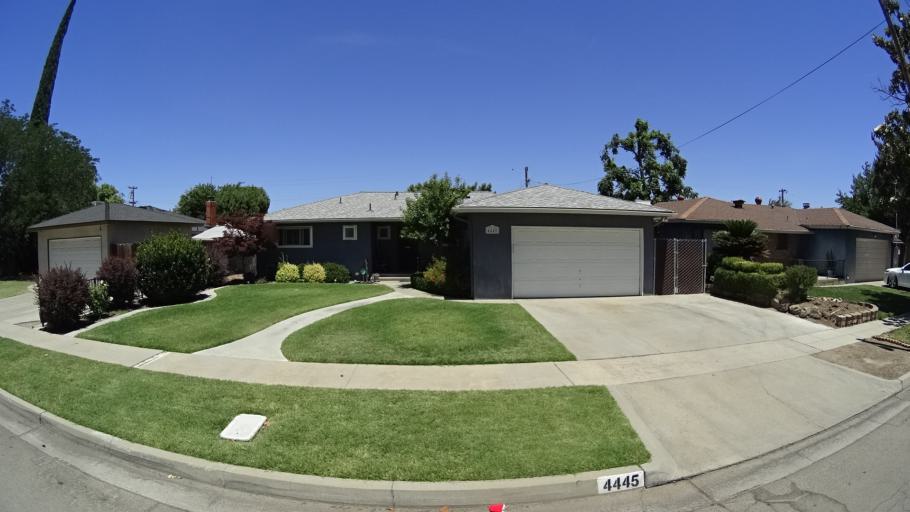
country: US
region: California
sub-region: Fresno County
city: Tarpey Village
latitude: 36.7988
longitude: -119.7509
